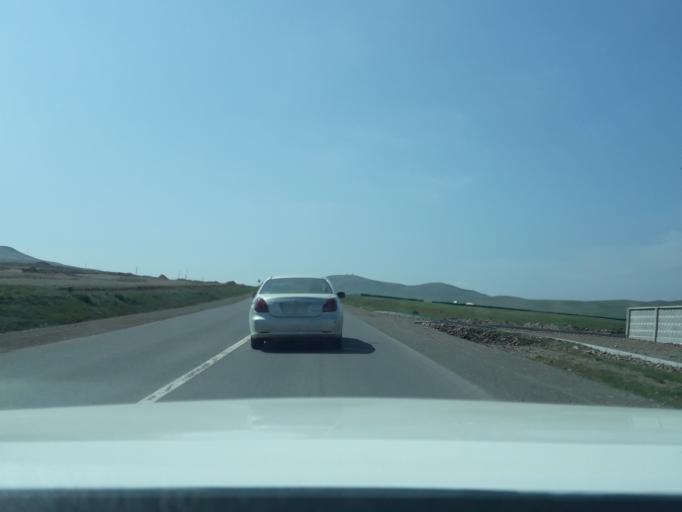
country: MN
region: Ulaanbaatar
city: Ulaanbaatar
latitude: 47.8156
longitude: 106.7556
